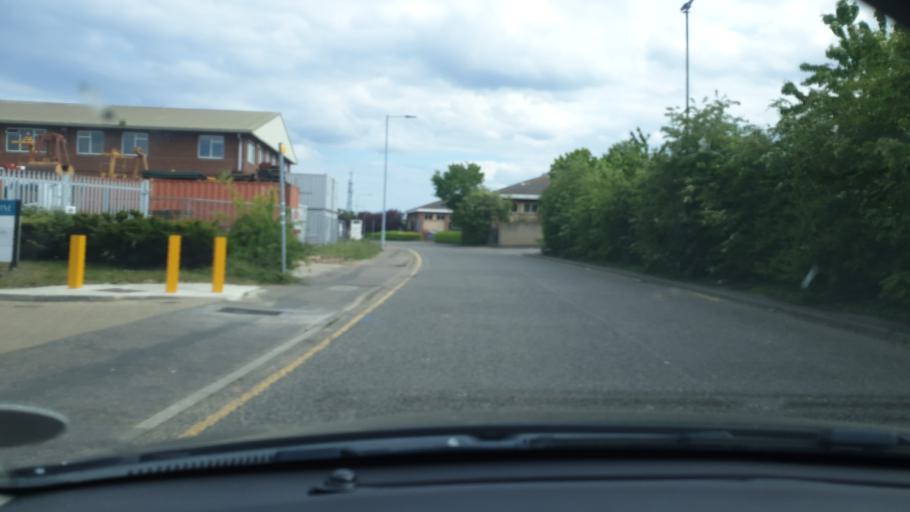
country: GB
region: England
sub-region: Essex
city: Colchester
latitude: 51.9203
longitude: 0.9228
